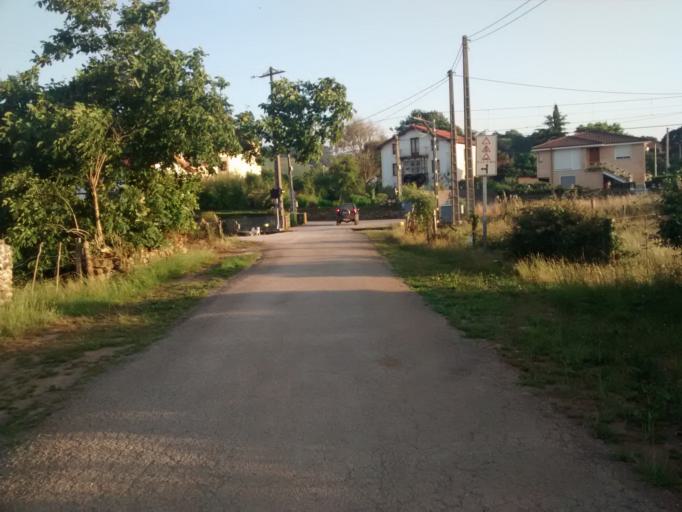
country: ES
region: Cantabria
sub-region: Provincia de Cantabria
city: Entrambasaguas
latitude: 43.3773
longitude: -3.7188
